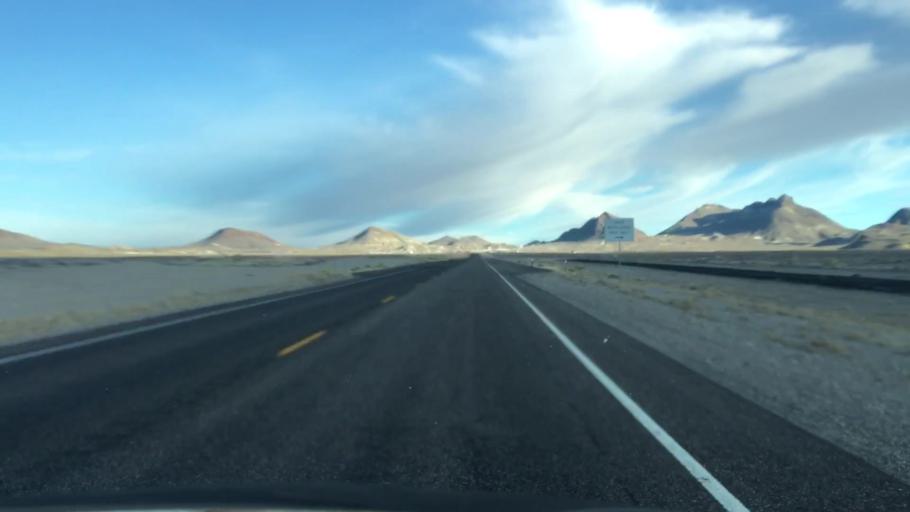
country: US
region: Nevada
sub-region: Nye County
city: Tonopah
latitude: 38.0865
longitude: -117.2865
